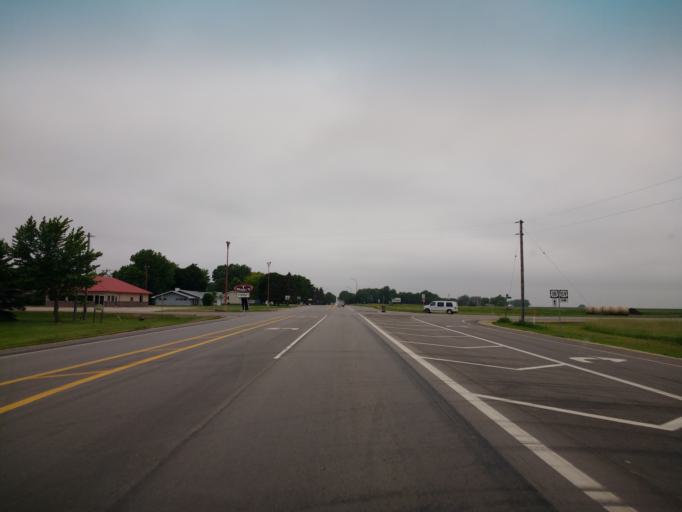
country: US
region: Iowa
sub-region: O'Brien County
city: Sanborn
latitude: 43.1861
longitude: -95.6431
